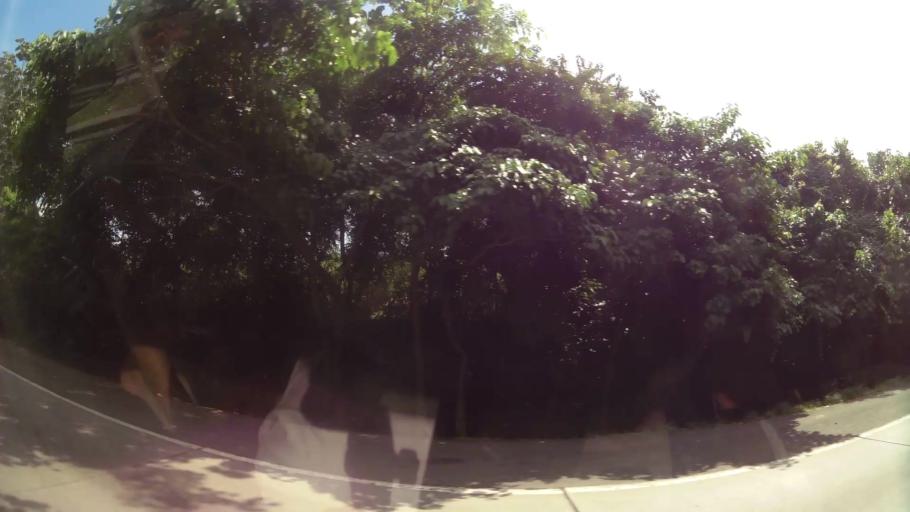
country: PA
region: Panama
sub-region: Distrito de Panama
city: Paraiso
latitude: 9.0272
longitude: -79.6054
